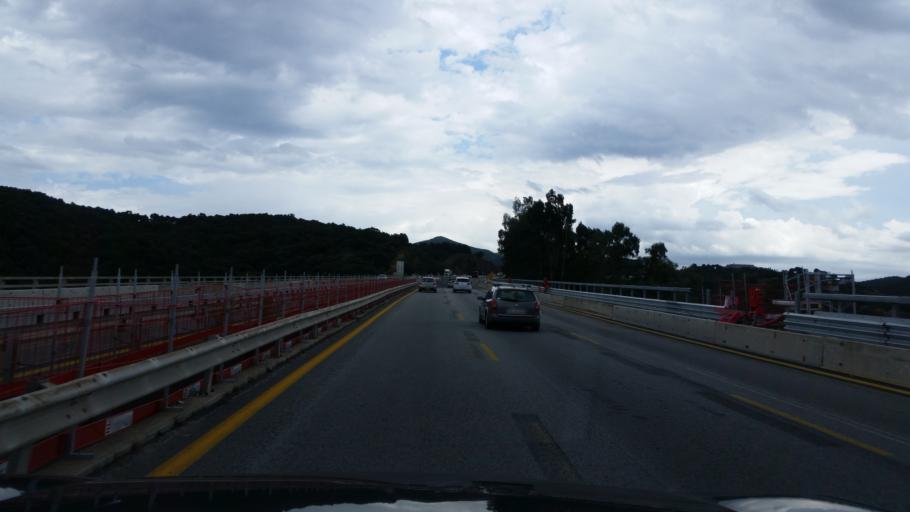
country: FR
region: Languedoc-Roussillon
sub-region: Departement des Pyrenees-Orientales
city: Maureillas-las-Illas
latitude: 42.4895
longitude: 2.8388
